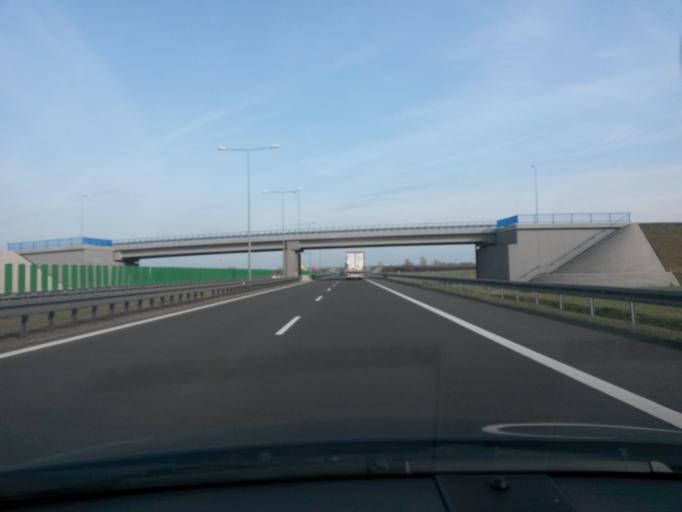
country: PL
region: Greater Poland Voivodeship
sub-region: Powiat slupecki
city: Strzalkowo
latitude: 52.2545
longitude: 17.8171
